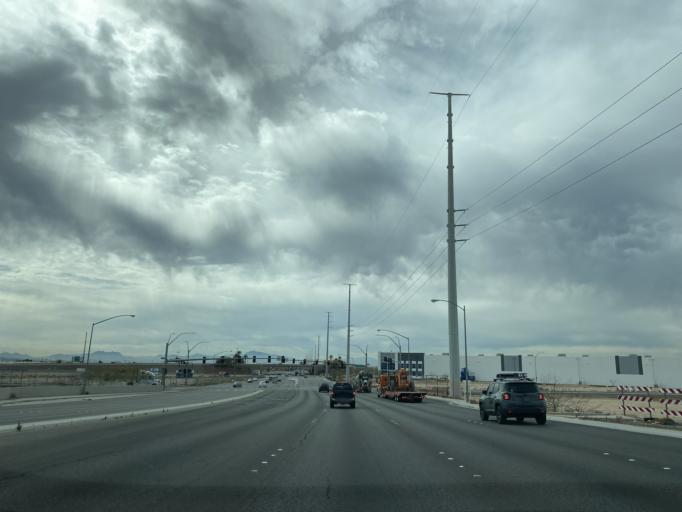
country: US
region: Nevada
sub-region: Clark County
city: Nellis Air Force Base
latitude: 36.2633
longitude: -115.0800
